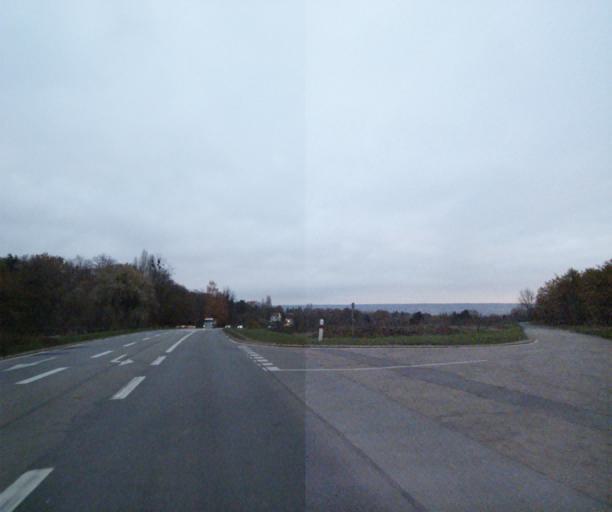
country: FR
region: Ile-de-France
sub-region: Departement des Yvelines
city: Villennes-sur-Seine
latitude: 48.9436
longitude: 1.9782
